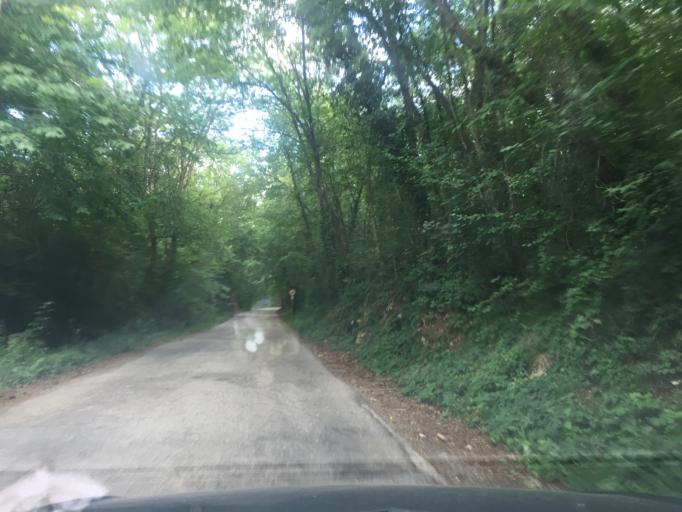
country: IT
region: Friuli Venezia Giulia
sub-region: Provincia di Gorizia
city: Savogna d'Isonzo
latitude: 45.8926
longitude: 13.5631
